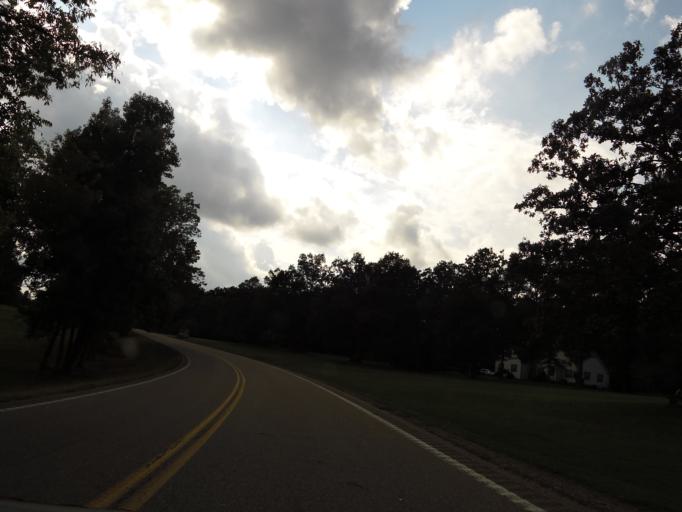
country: US
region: Mississippi
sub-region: Alcorn County
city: Farmington
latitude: 35.0639
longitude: -88.4132
